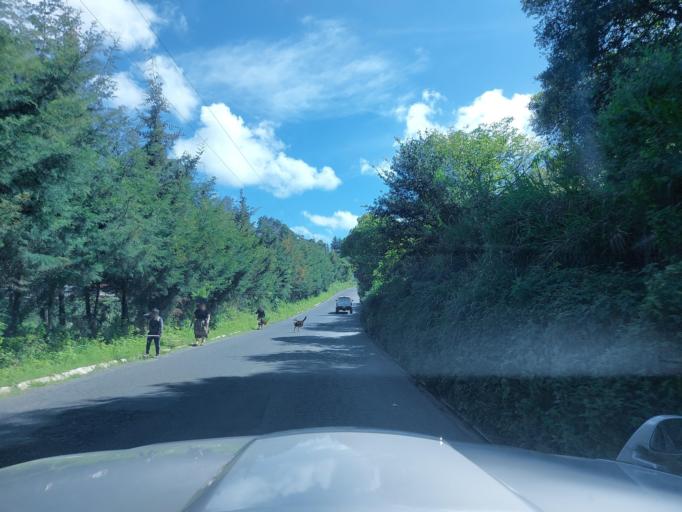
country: GT
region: Chimaltenango
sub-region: Municipio de San Juan Comalapa
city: Comalapa
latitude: 14.7171
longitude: -90.8892
